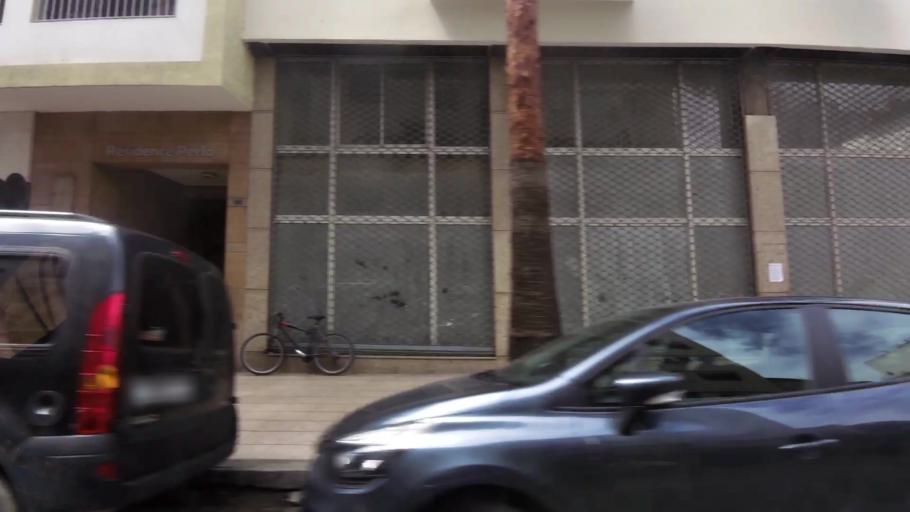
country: MA
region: Grand Casablanca
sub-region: Casablanca
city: Casablanca
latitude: 33.5876
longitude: -7.6310
